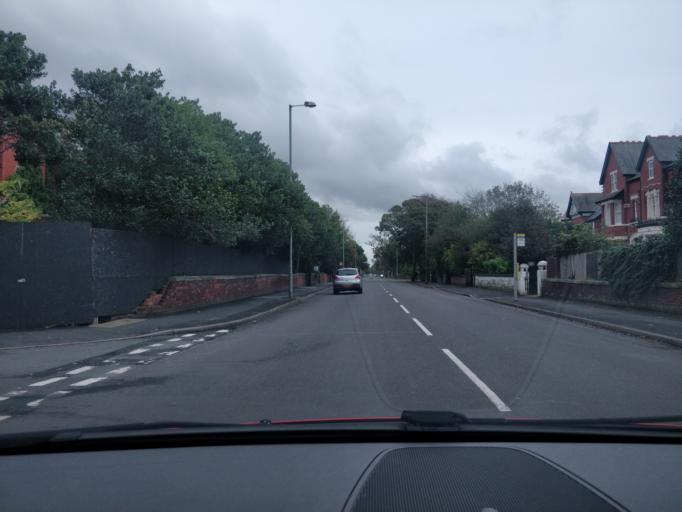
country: GB
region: England
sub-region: Sefton
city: Southport
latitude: 53.6392
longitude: -2.9910
